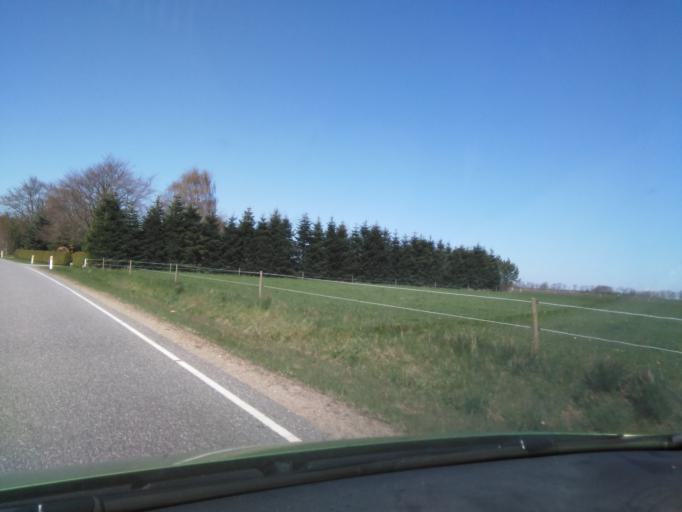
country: DK
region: South Denmark
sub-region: Billund Kommune
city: Grindsted
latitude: 55.6999
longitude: 8.8319
